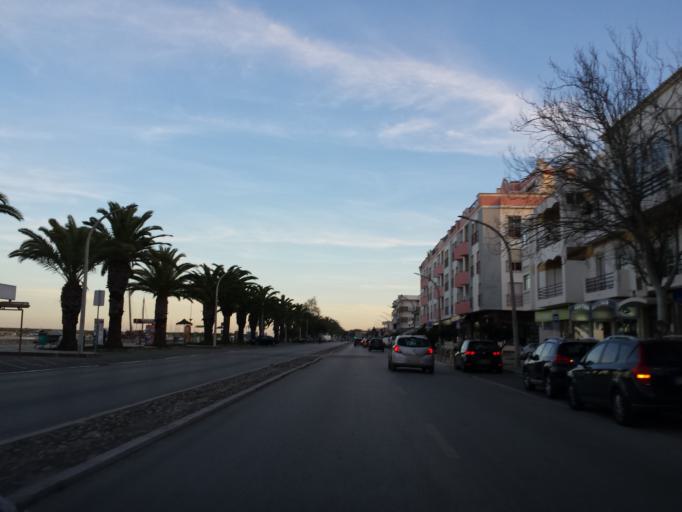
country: PT
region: Faro
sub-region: Lagos
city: Lagos
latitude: 37.1073
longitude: -8.6750
